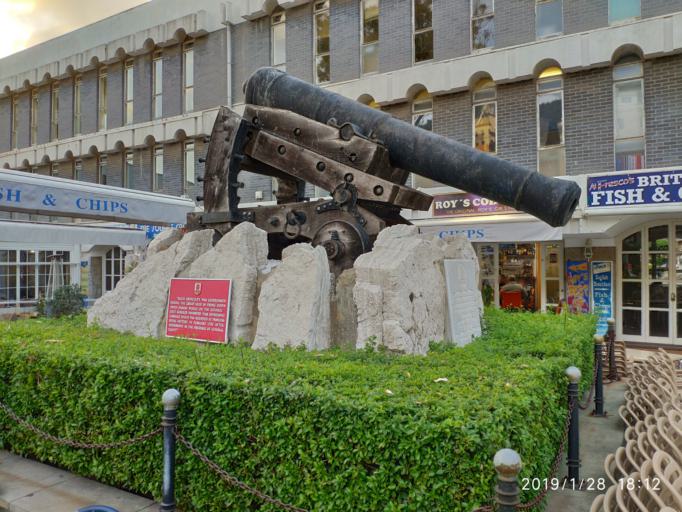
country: GI
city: Gibraltar
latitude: 36.1449
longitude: -5.3531
